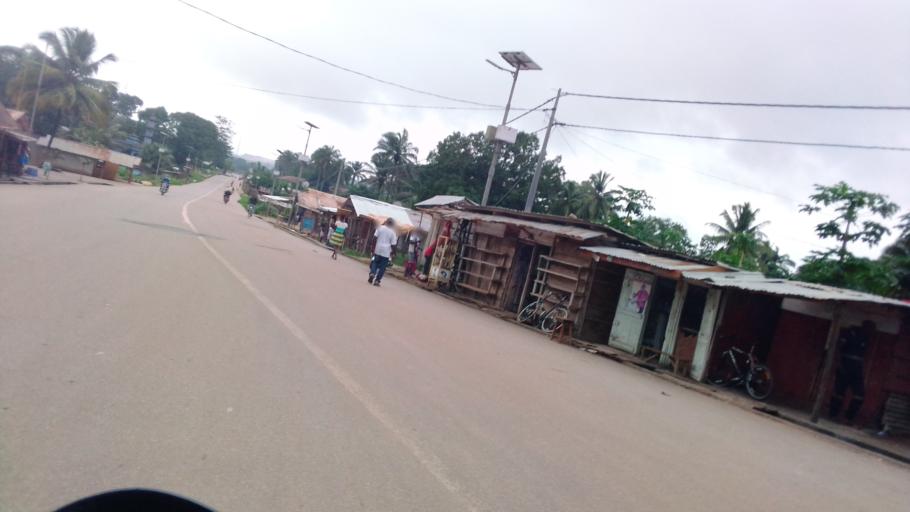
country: SL
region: Northern Province
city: Lunsar
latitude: 8.6874
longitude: -12.5425
